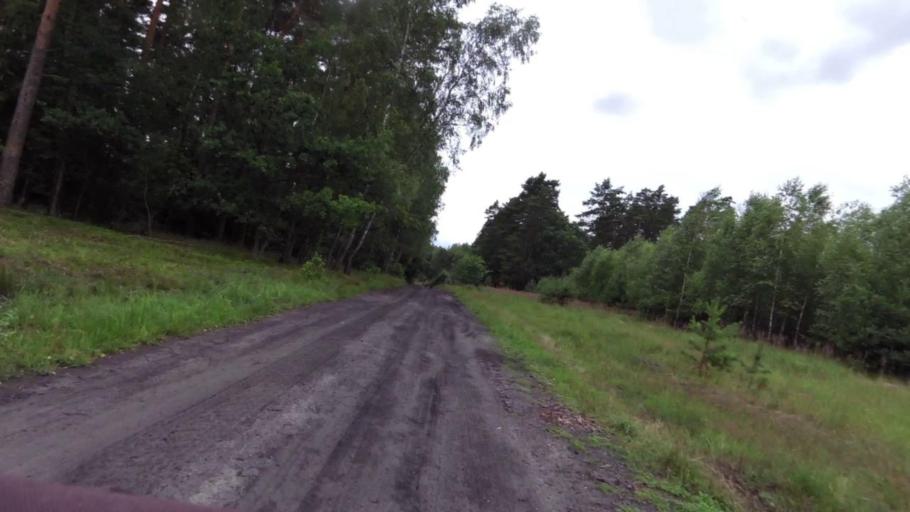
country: PL
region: West Pomeranian Voivodeship
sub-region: Powiat mysliborski
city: Debno
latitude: 52.8101
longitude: 14.6688
